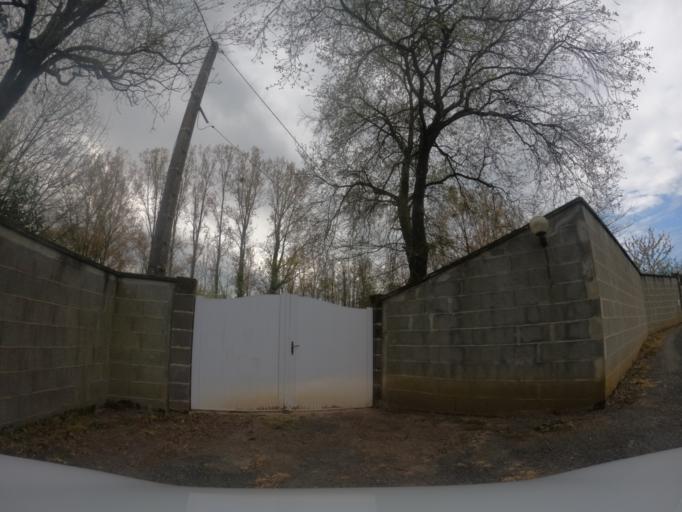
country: FR
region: Pays de la Loire
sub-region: Departement de la Vendee
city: Le Champ-Saint-Pere
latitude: 46.5285
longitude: -1.3300
